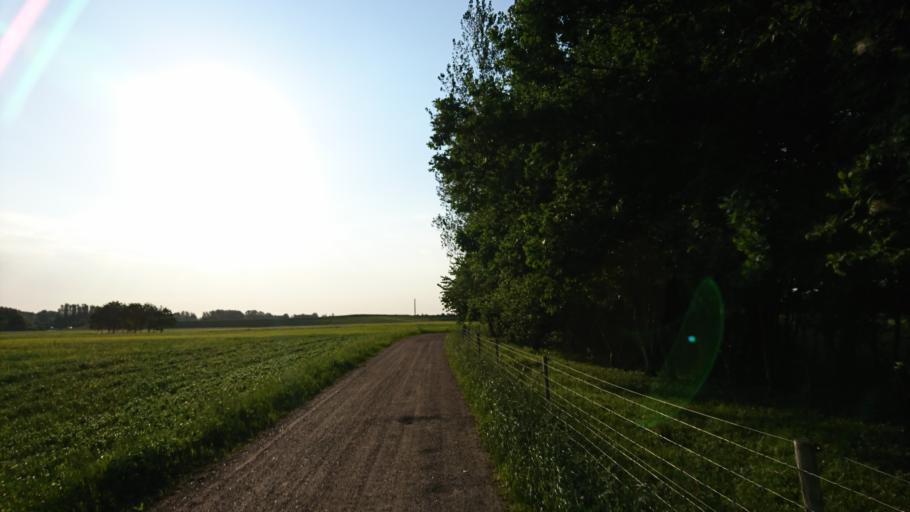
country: DK
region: Capital Region
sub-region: Ballerup Kommune
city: Ballerup
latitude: 55.7084
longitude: 12.3581
